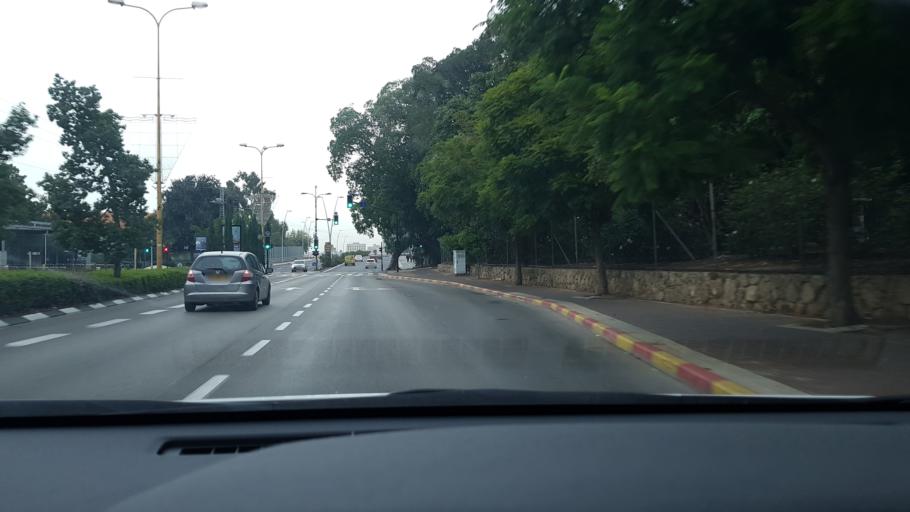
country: IL
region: Central District
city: Ness Ziona
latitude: 31.9055
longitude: 34.8065
